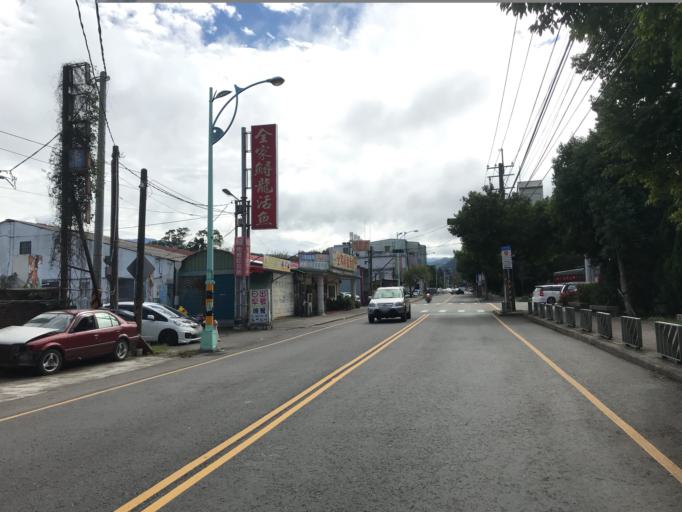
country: TW
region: Taiwan
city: Daxi
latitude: 24.8414
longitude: 121.2406
